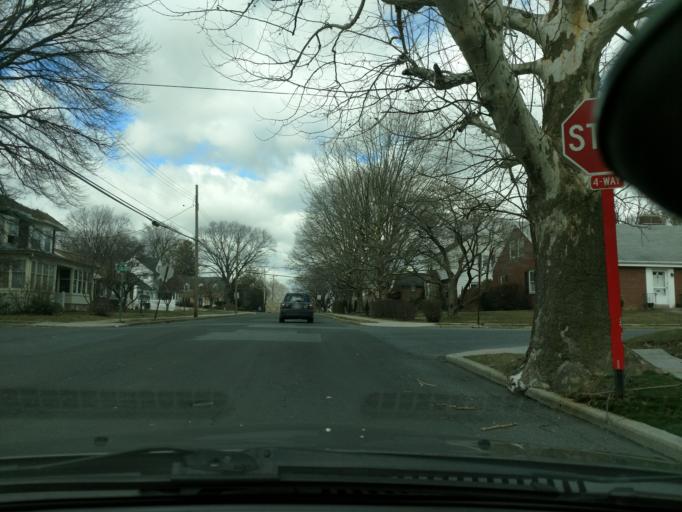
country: US
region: Pennsylvania
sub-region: Lebanon County
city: Lebanon
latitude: 40.3363
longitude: -76.4062
